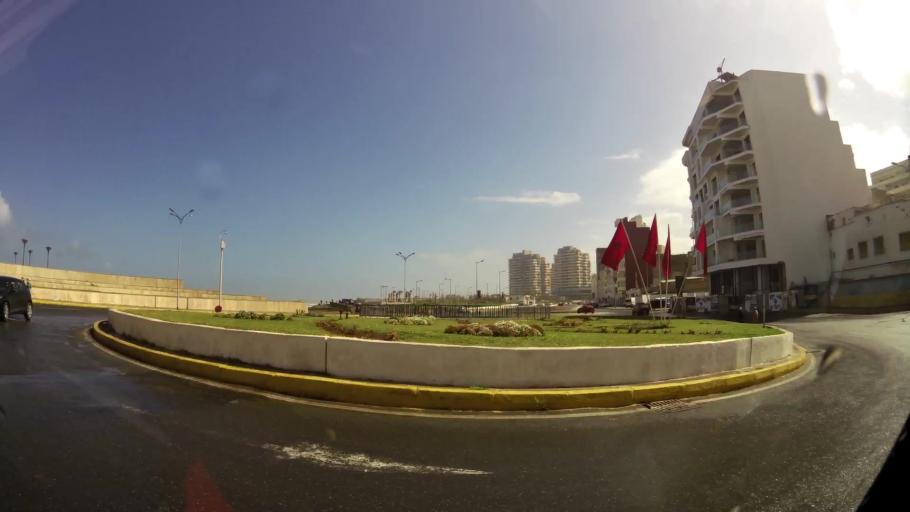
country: MA
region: Grand Casablanca
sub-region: Casablanca
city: Casablanca
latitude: 33.6075
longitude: -7.6305
